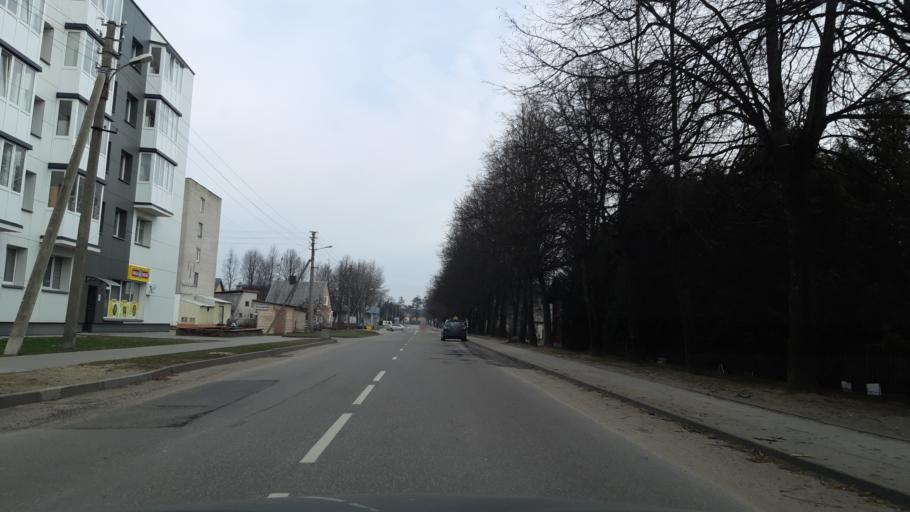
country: LT
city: Kazlu Ruda
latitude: 54.7510
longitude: 23.4896
